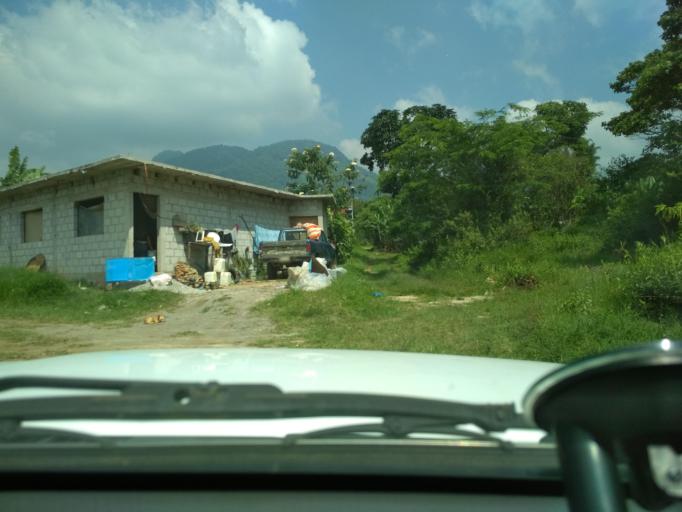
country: MX
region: Veracruz
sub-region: Fortin
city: Santa Lucia Potrerillo
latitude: 18.9668
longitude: -97.0248
